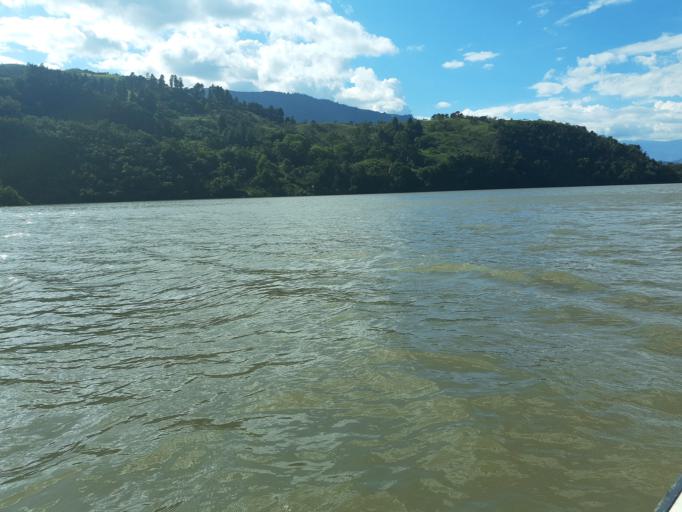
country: CO
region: Boyaca
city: Chivor
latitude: 4.9398
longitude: -73.3155
